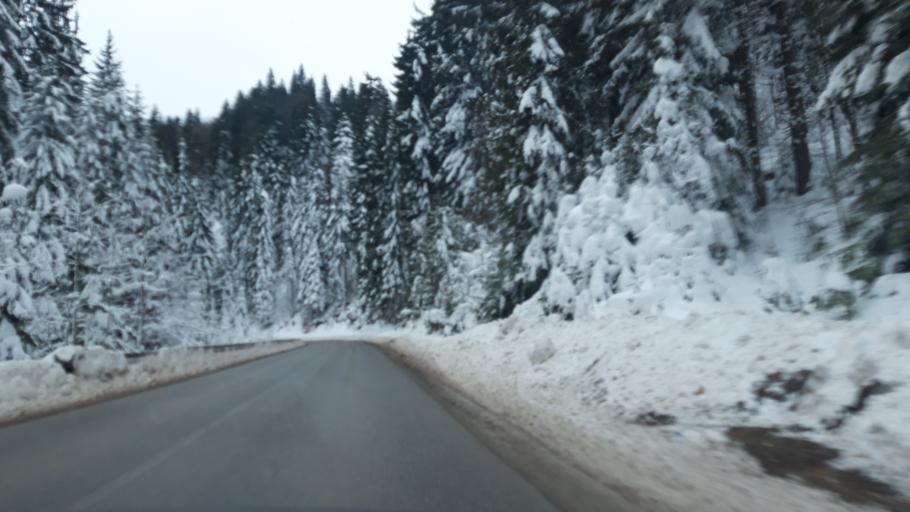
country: BA
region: Republika Srpska
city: Koran
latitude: 43.7459
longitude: 18.5652
